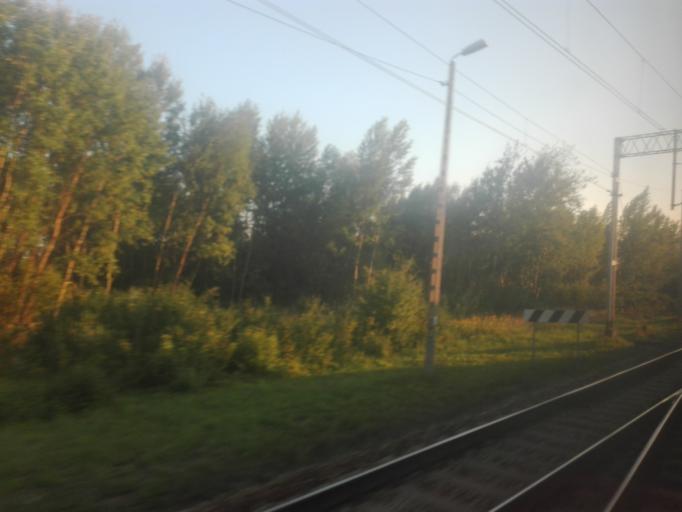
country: PL
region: Masovian Voivodeship
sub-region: Powiat warszawski zachodni
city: Bieniewice
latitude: 52.1863
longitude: 20.5896
